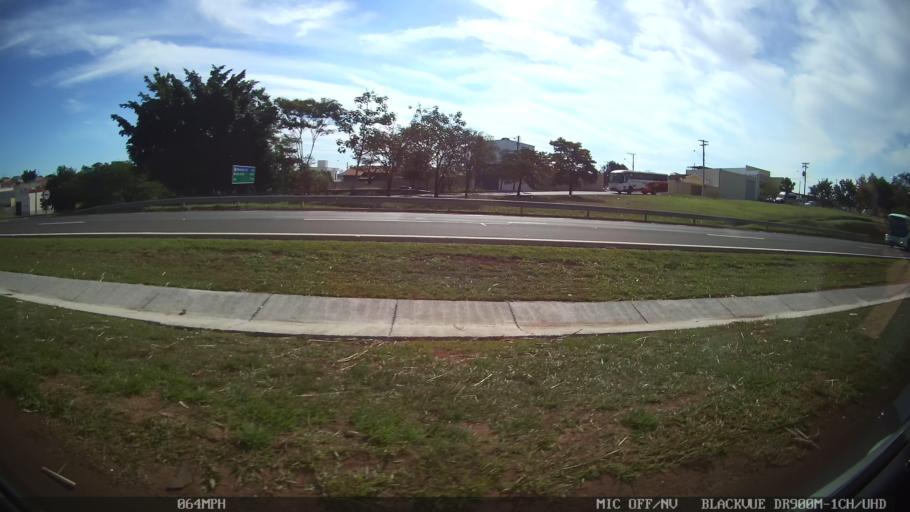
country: BR
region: Sao Paulo
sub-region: Araraquara
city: Araraquara
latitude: -21.8048
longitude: -48.1494
